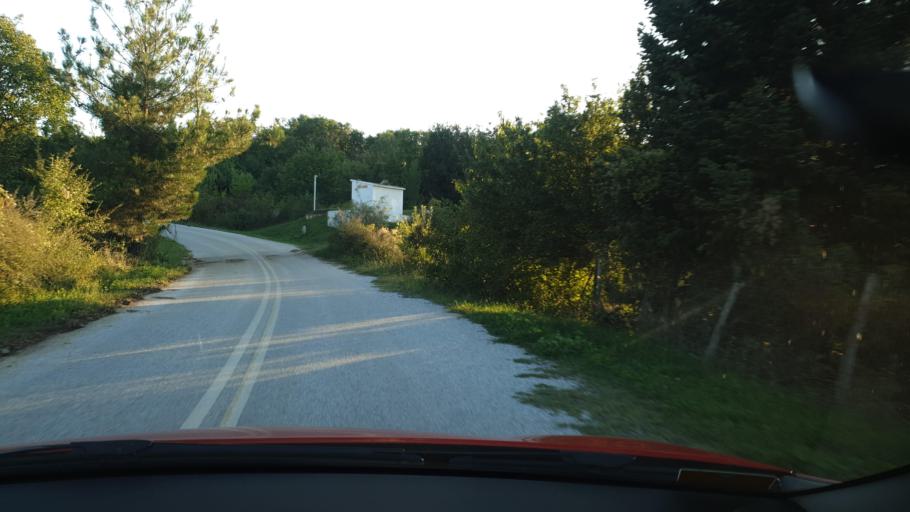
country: GR
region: Central Macedonia
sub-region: Nomos Chalkidikis
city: Galatista
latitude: 40.5199
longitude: 23.2755
